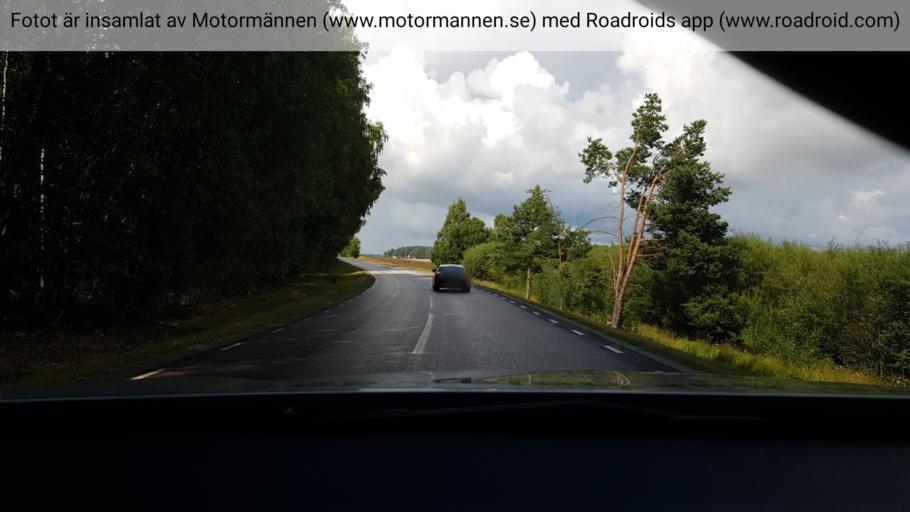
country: SE
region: Stockholm
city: Stenhamra
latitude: 59.3563
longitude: 17.6243
